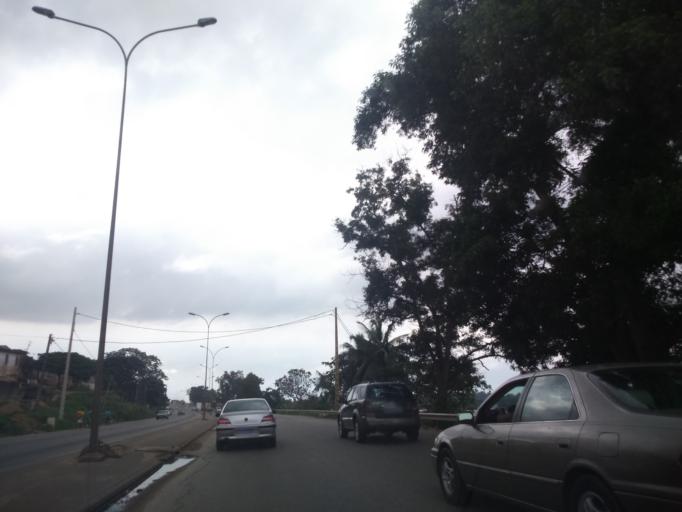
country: CI
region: Lagunes
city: Abidjan
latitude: 5.3538
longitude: -4.0403
